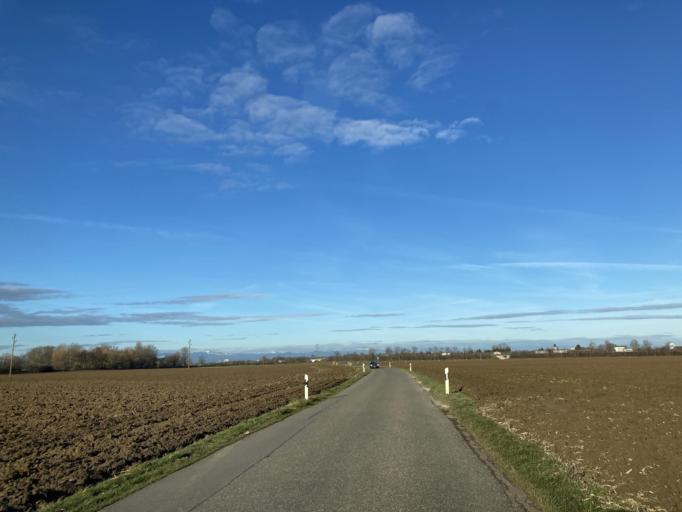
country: DE
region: Baden-Wuerttemberg
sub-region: Freiburg Region
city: Unterkrozingen
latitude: 47.9490
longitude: 7.6836
